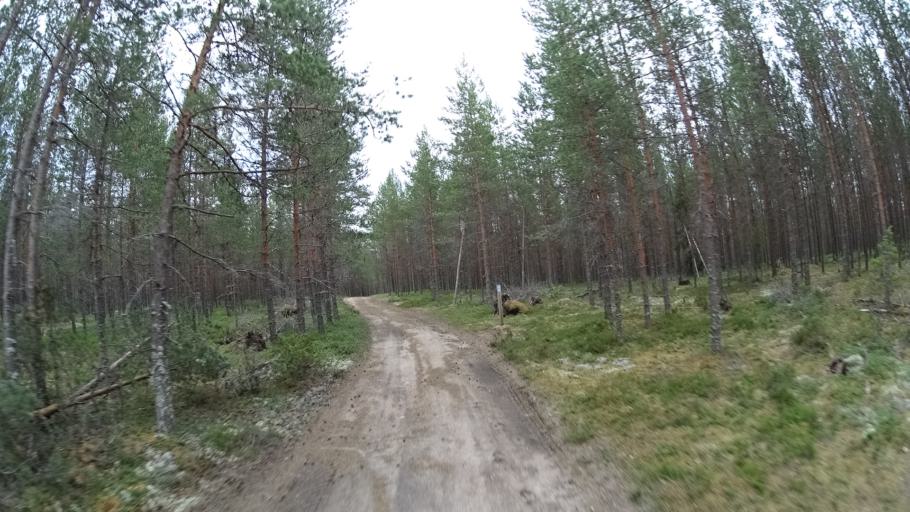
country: FI
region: Satakunta
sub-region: Pohjois-Satakunta
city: Jaemijaervi
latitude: 61.7617
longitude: 22.7752
